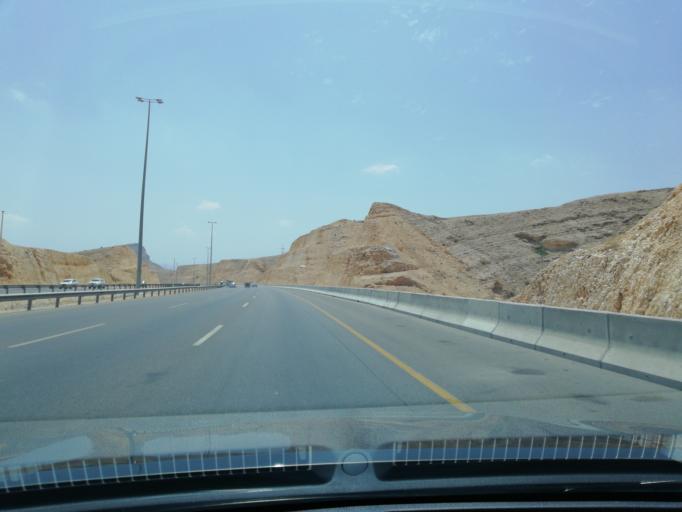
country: OM
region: Muhafazat Masqat
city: As Sib al Jadidah
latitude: 23.5470
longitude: 58.2382
